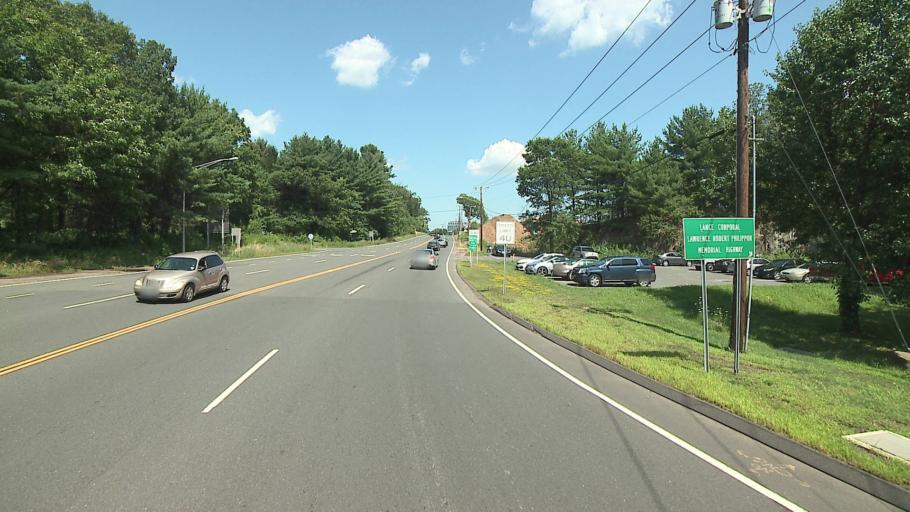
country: US
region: Connecticut
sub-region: Hartford County
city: Farmington
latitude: 41.7243
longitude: -72.8082
